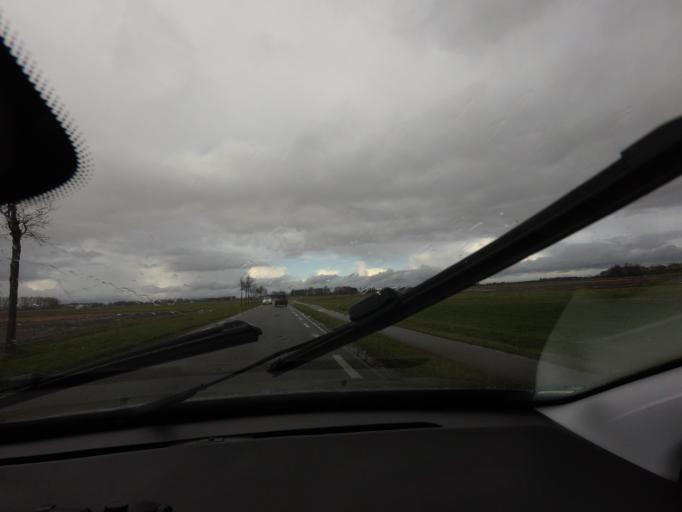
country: NL
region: Groningen
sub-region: Gemeente Veendam
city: Veendam
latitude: 53.0329
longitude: 6.8087
